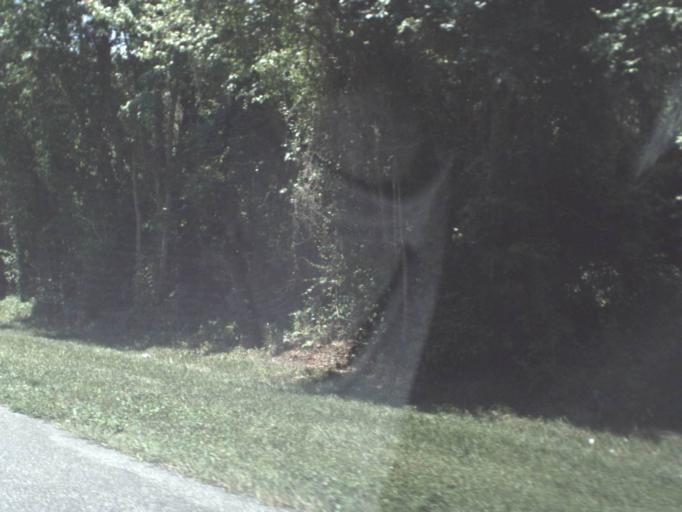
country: US
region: Florida
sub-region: Putnam County
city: Crescent City
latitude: 29.4659
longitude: -81.5266
